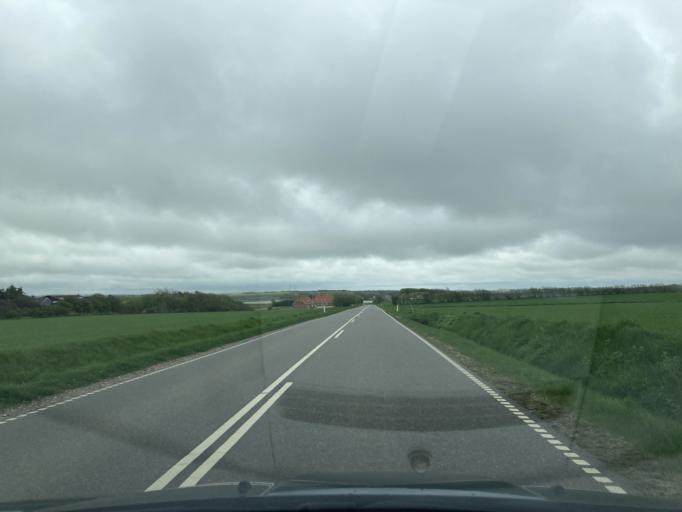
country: DK
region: North Denmark
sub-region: Thisted Kommune
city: Hurup
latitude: 56.8212
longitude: 8.3516
